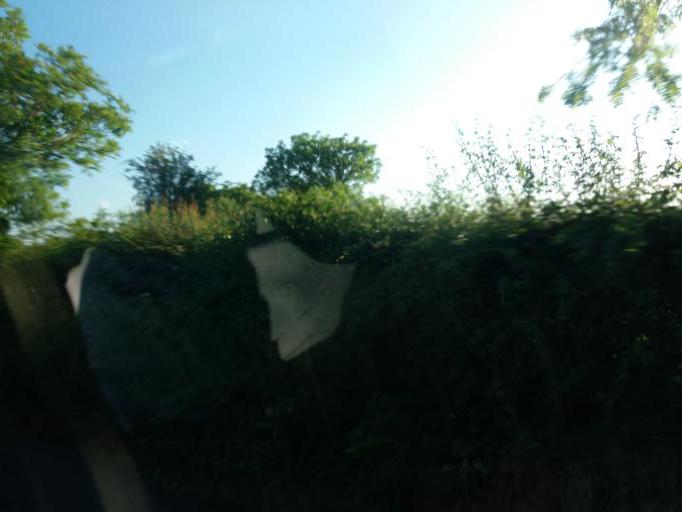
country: IE
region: Leinster
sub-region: An Mhi
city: Ashbourne
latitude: 53.5709
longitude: -6.3513
